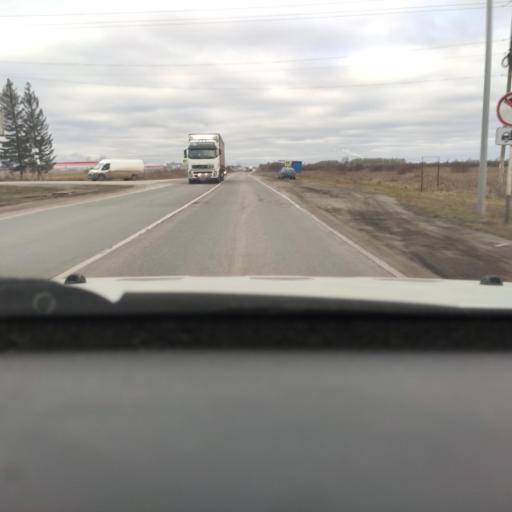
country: RU
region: Perm
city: Froly
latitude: 57.8951
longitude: 56.2637
